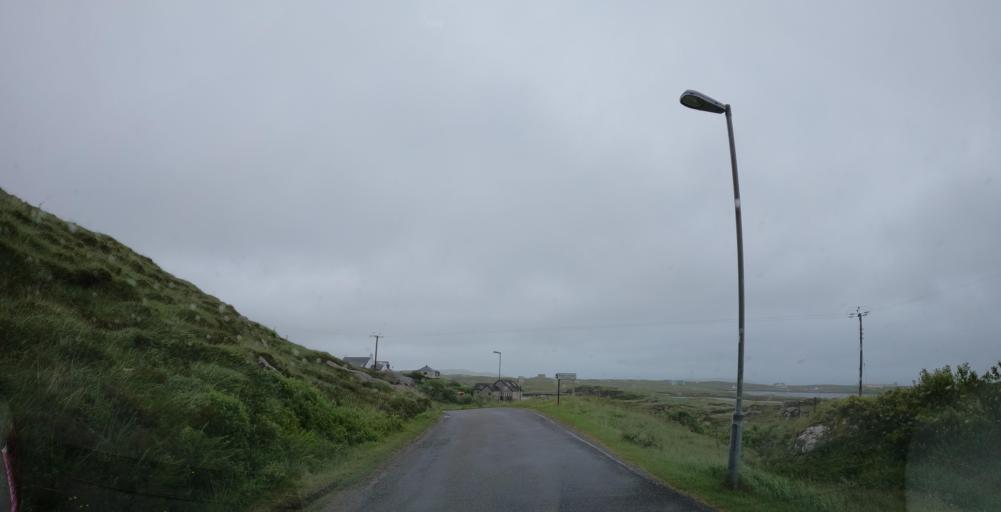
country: GB
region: Scotland
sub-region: Eilean Siar
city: Barra
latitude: 56.9966
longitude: -7.4191
